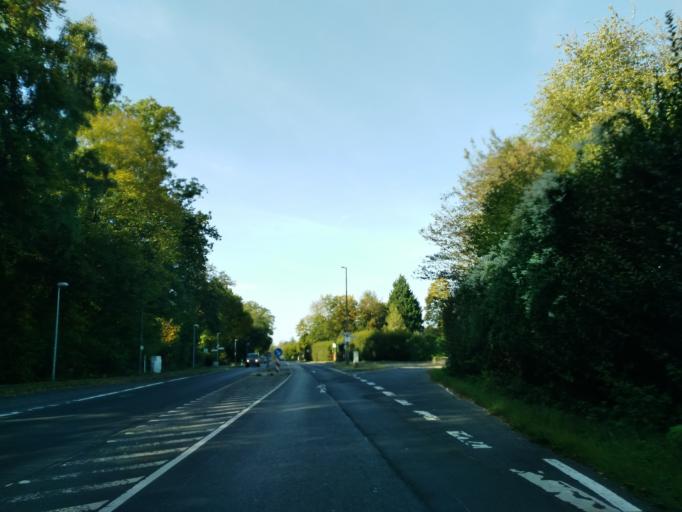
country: DE
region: North Rhine-Westphalia
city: Sankt Augustin
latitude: 50.7518
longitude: 7.2191
